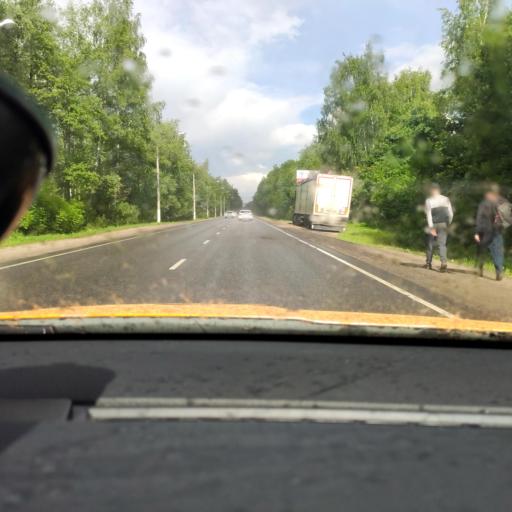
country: RU
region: Moskovskaya
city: Stupino
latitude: 54.8852
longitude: 38.0332
